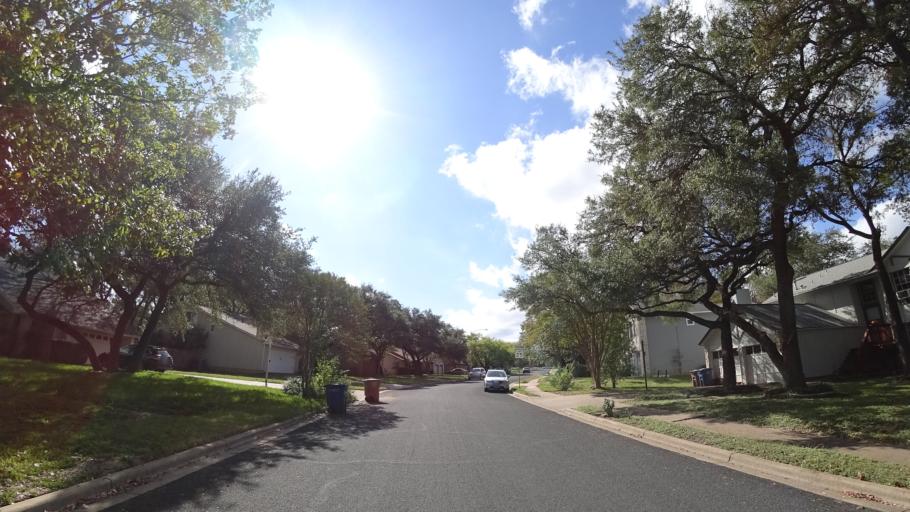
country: US
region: Texas
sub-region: Travis County
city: Wells Branch
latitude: 30.4234
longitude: -97.7198
